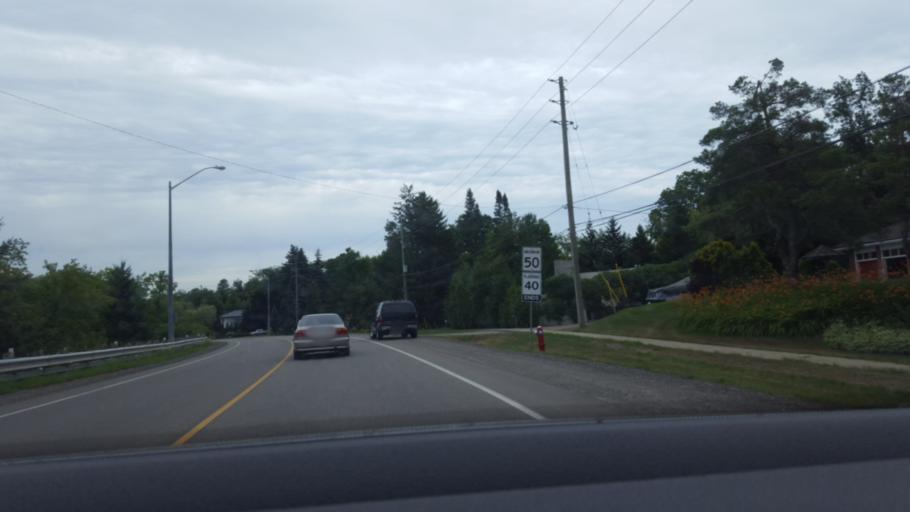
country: CA
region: Ontario
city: Brampton
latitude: 43.6416
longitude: -79.8069
